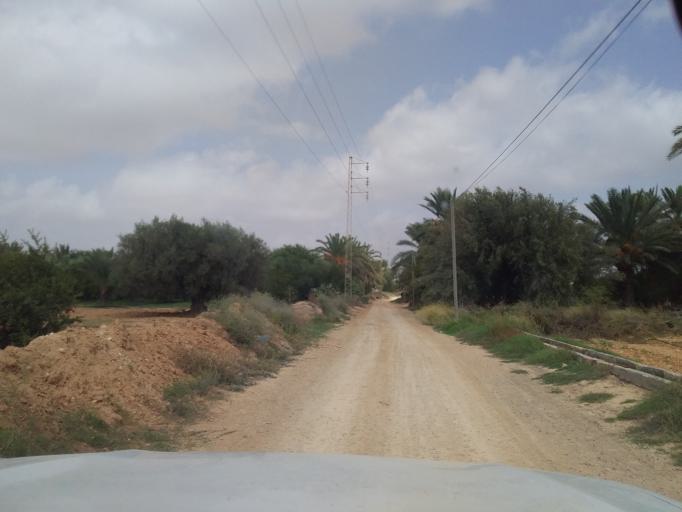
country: TN
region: Madanin
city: Medenine
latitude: 33.6243
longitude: 10.3121
